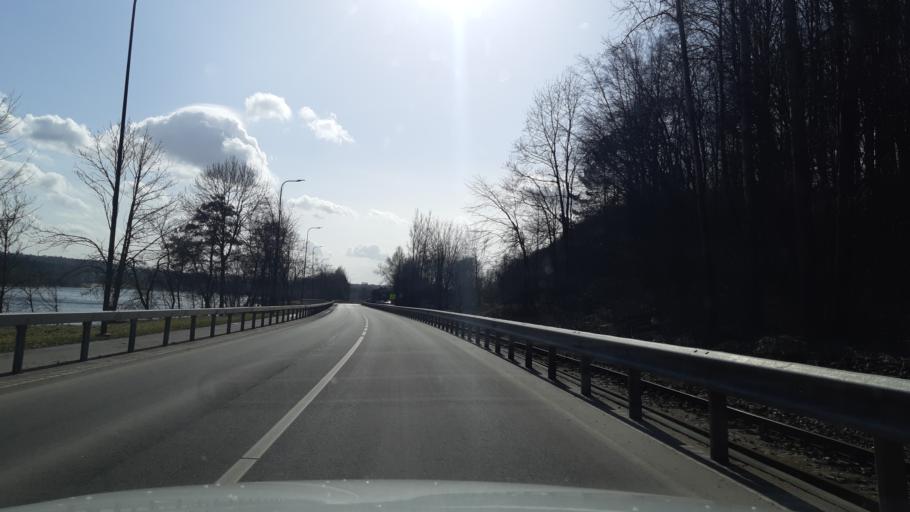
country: LT
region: Kauno apskritis
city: Dainava (Kaunas)
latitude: 54.8840
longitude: 23.9562
